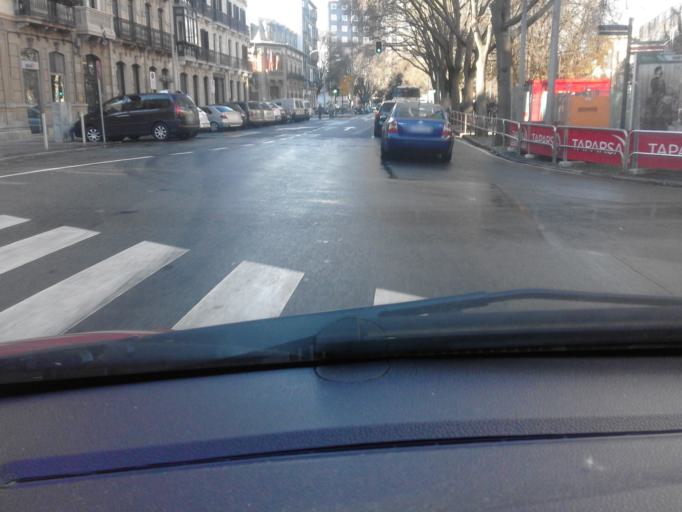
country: ES
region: Navarre
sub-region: Provincia de Navarra
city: Primer Ensanche
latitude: 42.8148
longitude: -1.6467
